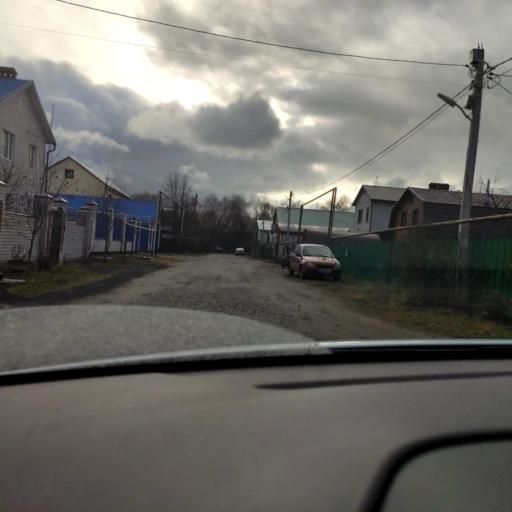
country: RU
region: Tatarstan
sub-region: Gorod Kazan'
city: Kazan
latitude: 55.8820
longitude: 49.0992
